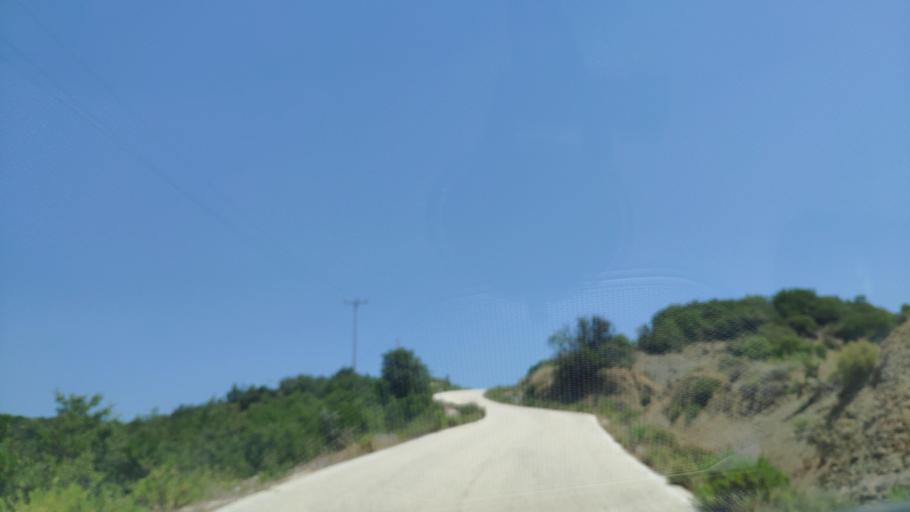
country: GR
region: West Greece
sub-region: Nomos Aitolias kai Akarnanias
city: Sardinia
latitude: 38.8762
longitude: 21.2800
